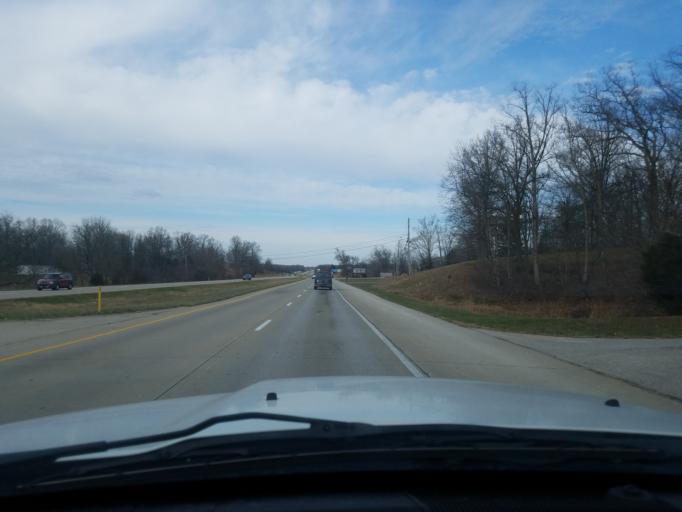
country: US
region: Indiana
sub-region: Lawrence County
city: Mitchell
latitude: 38.7760
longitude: -86.5027
